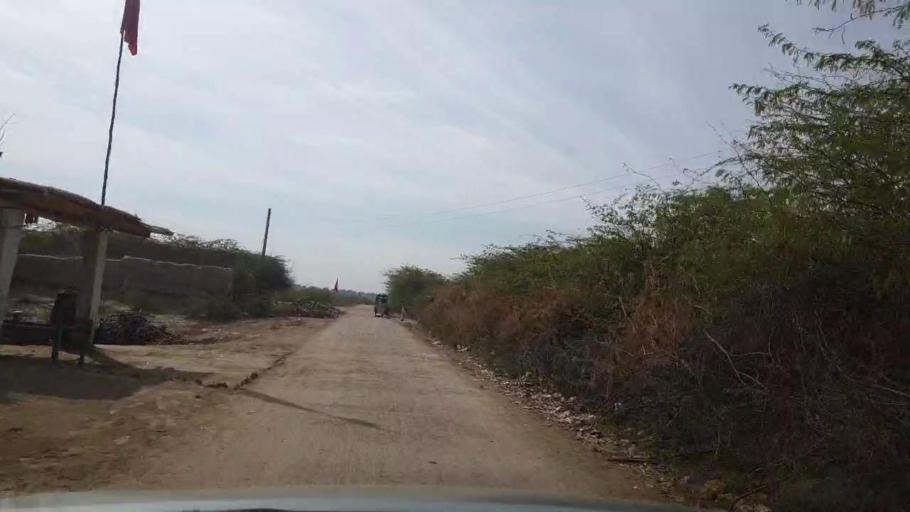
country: PK
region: Sindh
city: Kunri
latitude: 25.1467
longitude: 69.6044
